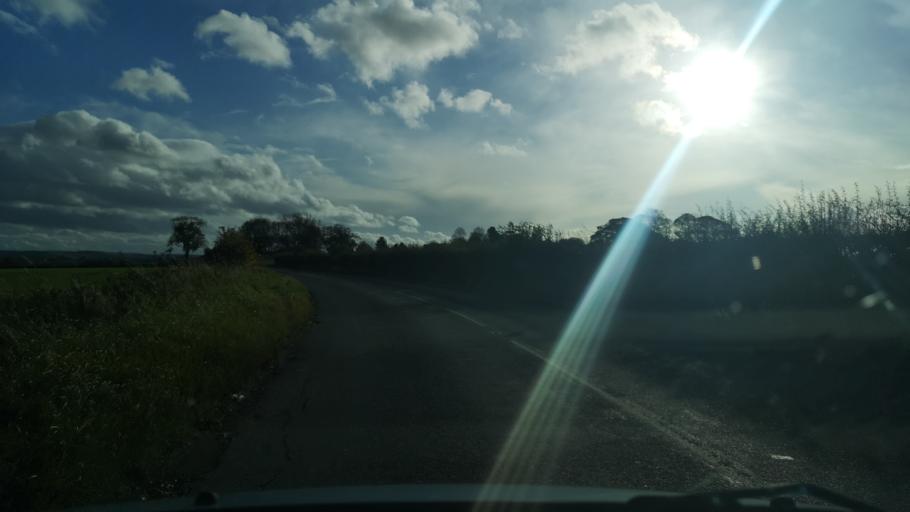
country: GB
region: England
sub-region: City and Borough of Wakefield
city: Middlestown
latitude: 53.6379
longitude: -1.6226
